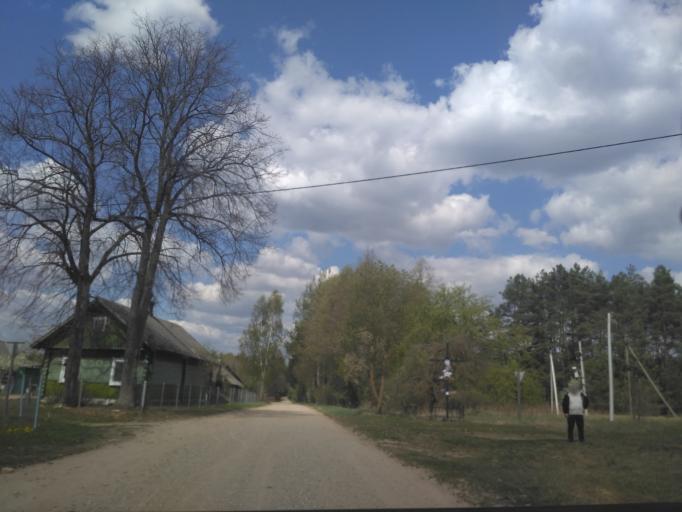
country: BY
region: Minsk
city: Il'ya
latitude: 54.2824
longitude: 27.2998
